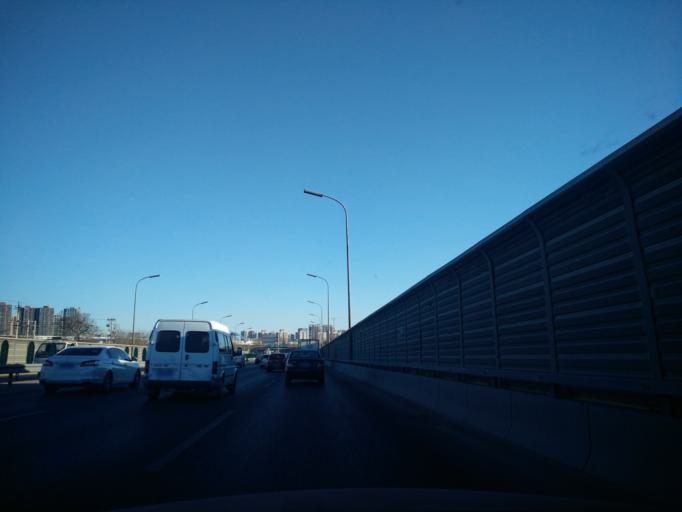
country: CN
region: Beijing
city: Lugu
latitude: 39.8843
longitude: 116.2038
